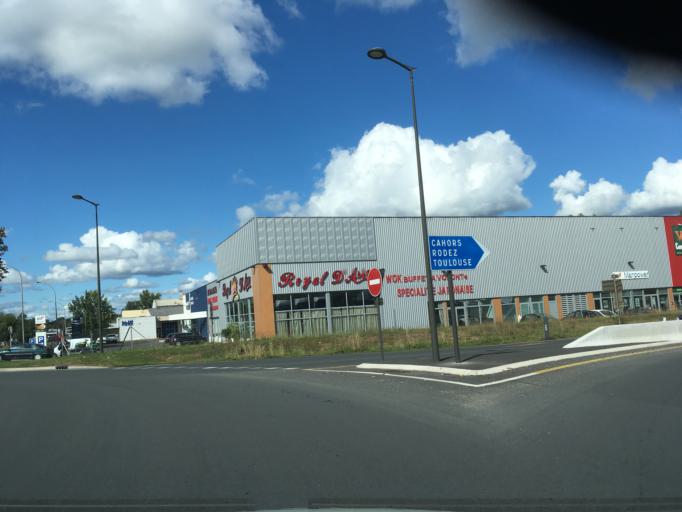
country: FR
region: Limousin
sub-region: Departement de la Correze
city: Saint-Pantaleon-de-Larche
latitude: 45.1490
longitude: 1.4823
